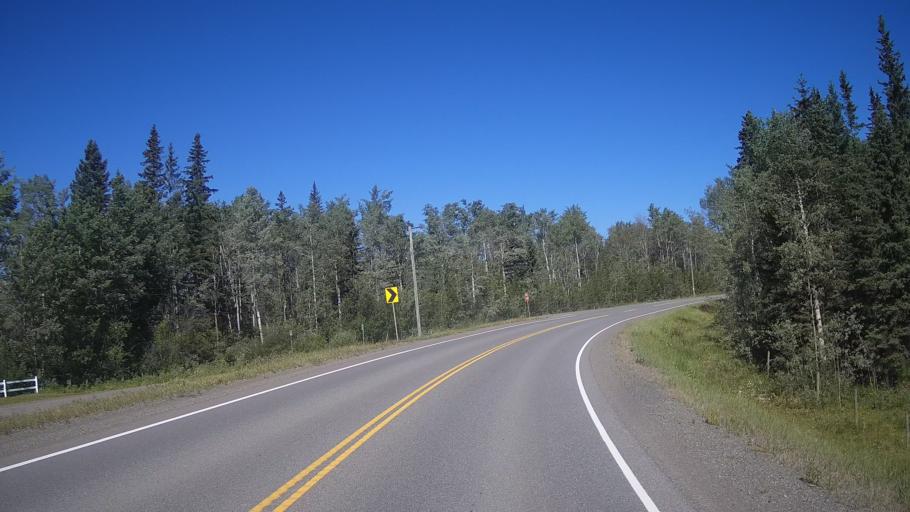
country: CA
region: British Columbia
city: Cache Creek
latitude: 51.5428
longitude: -120.9098
